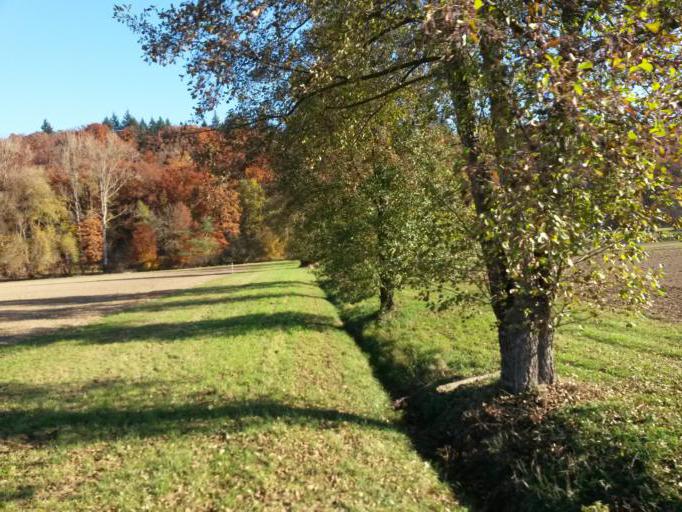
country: DE
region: Baden-Wuerttemberg
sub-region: Karlsruhe Region
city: Konigsbach-Stein
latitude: 48.9239
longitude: 8.5862
